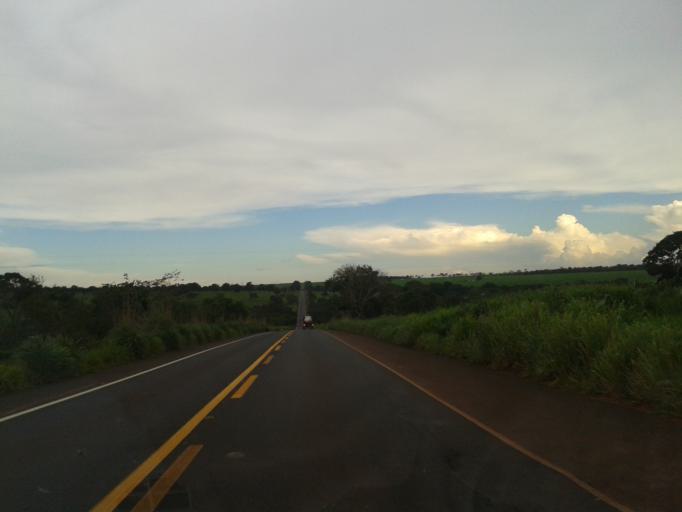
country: BR
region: Minas Gerais
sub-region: Santa Vitoria
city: Santa Vitoria
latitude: -18.9056
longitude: -50.2050
